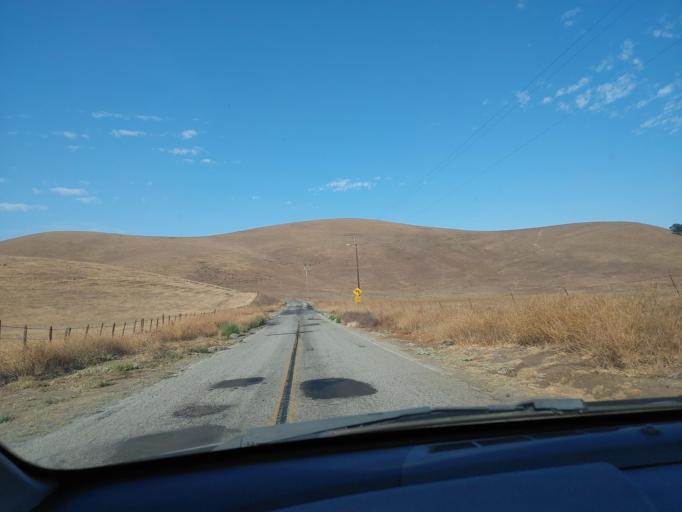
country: US
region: California
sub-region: San Benito County
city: Ridgemark
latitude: 36.7993
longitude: -121.3092
